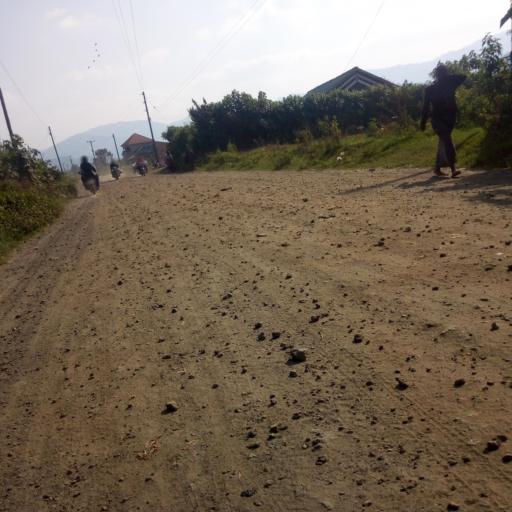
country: UG
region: Western Region
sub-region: Kisoro District
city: Kisoro
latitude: -1.2431
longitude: 29.7138
